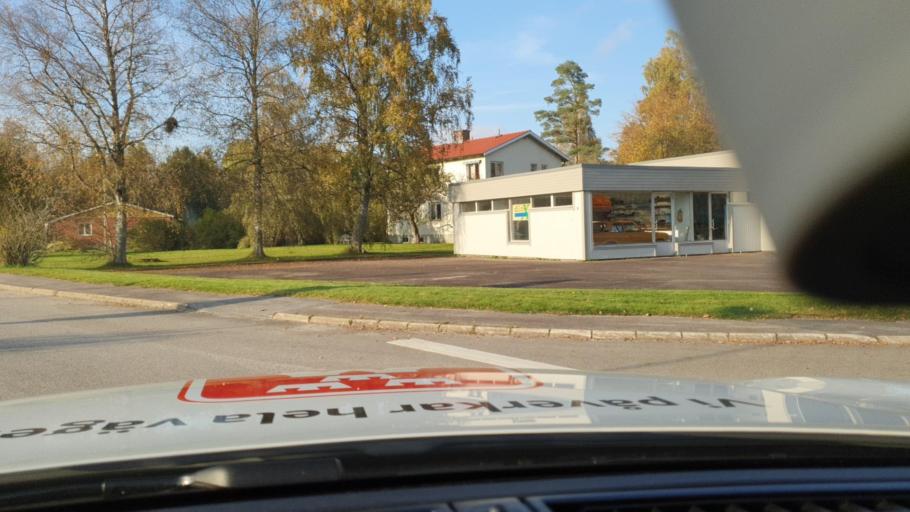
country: SE
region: Kronoberg
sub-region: Ljungby Kommun
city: Lagan
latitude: 56.9710
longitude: 13.9451
